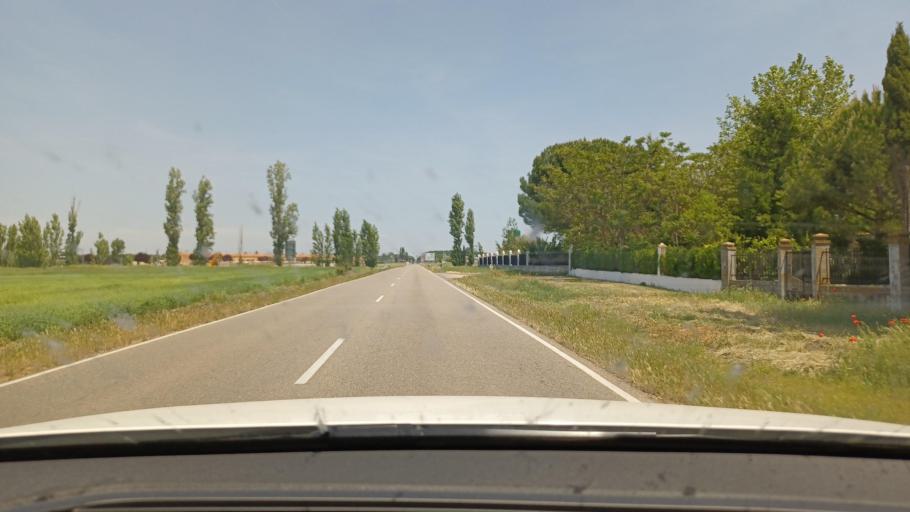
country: ES
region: Castille and Leon
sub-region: Provincia de Valladolid
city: Aldeamayor de San Martin
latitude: 41.5217
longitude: -4.6317
